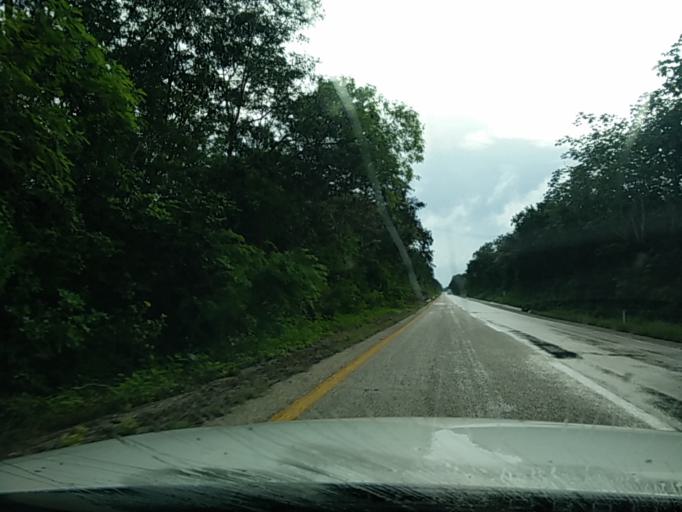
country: MX
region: Yucatan
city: Tunkas
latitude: 20.7539
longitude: -88.7390
